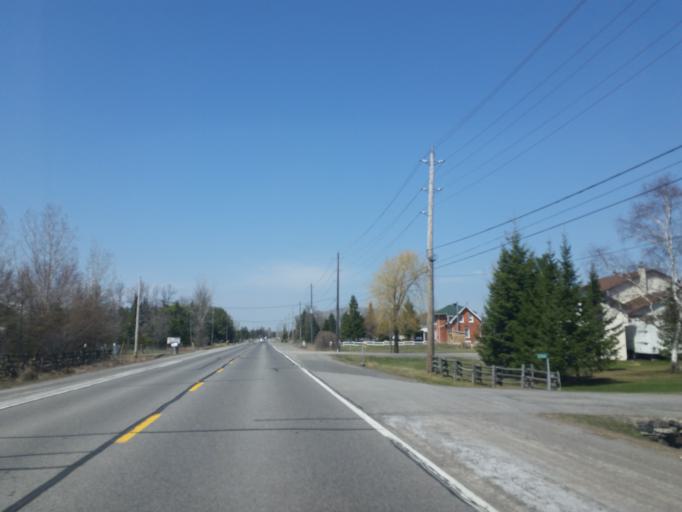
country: CA
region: Ontario
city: Bells Corners
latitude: 45.4443
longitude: -76.0510
